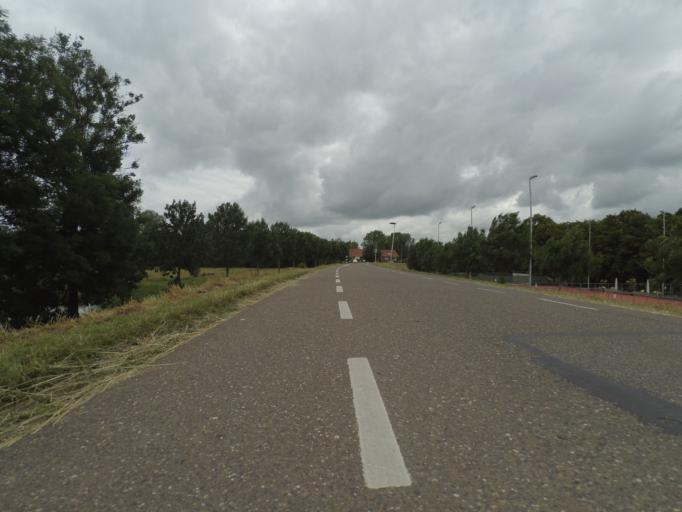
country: NL
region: Gelderland
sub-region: Gemeente Culemborg
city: Culemborg
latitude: 51.9579
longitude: 5.2199
